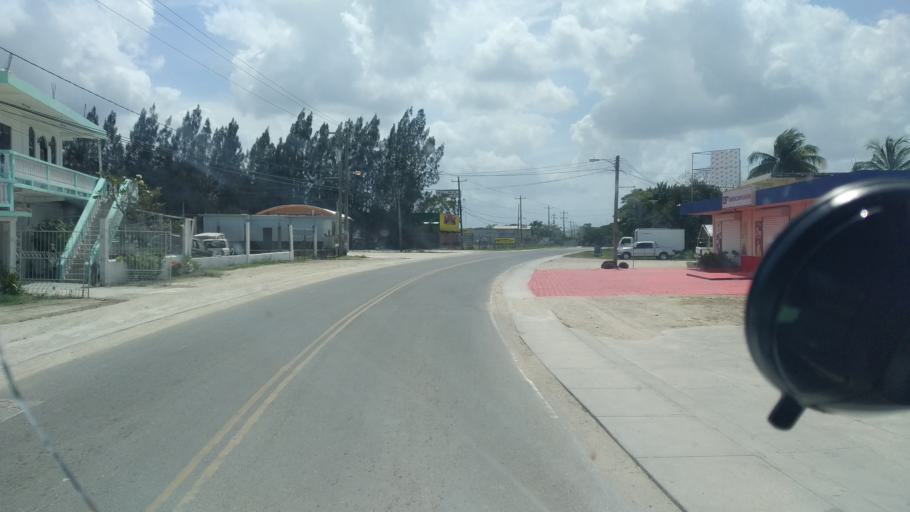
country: BZ
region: Orange Walk
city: Orange Walk
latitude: 18.0659
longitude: -88.5712
